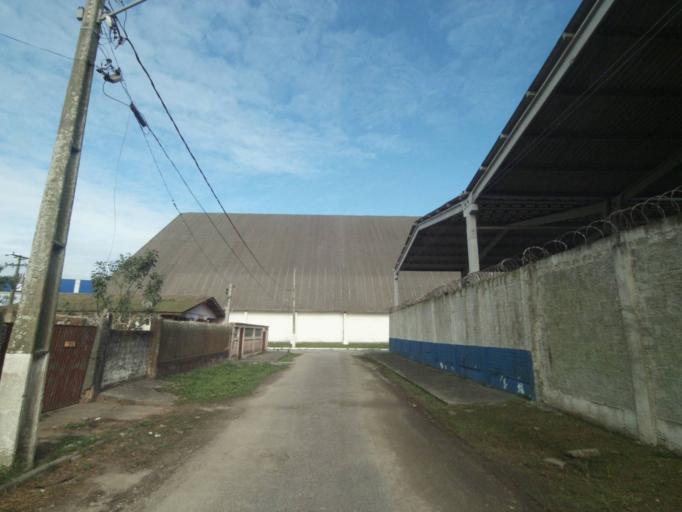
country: BR
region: Parana
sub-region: Paranagua
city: Paranagua
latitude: -25.5071
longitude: -48.5246
